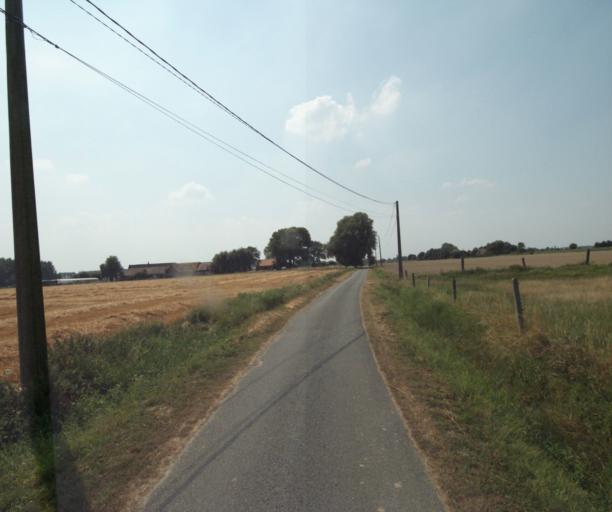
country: FR
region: Nord-Pas-de-Calais
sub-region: Departement du Nord
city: Wambrechies
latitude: 50.7127
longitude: 3.0418
